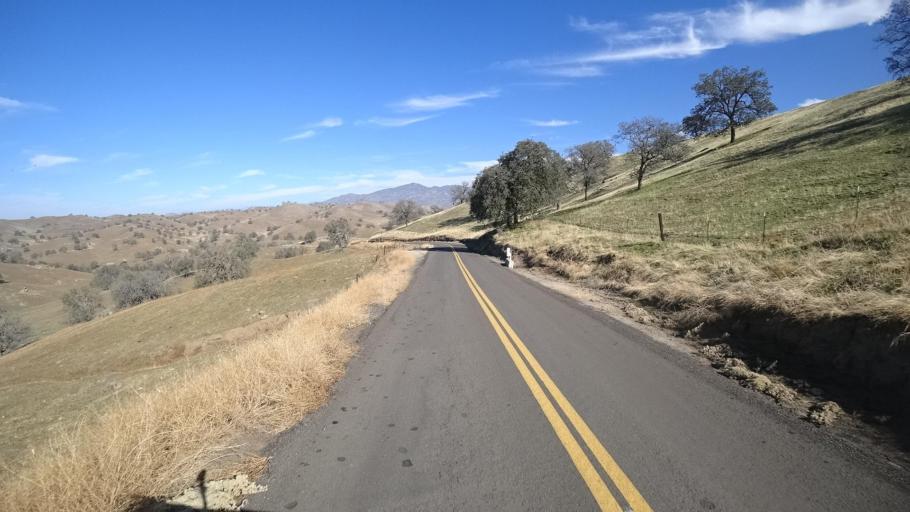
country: US
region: California
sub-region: Tulare County
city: Richgrove
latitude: 35.6952
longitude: -118.8601
